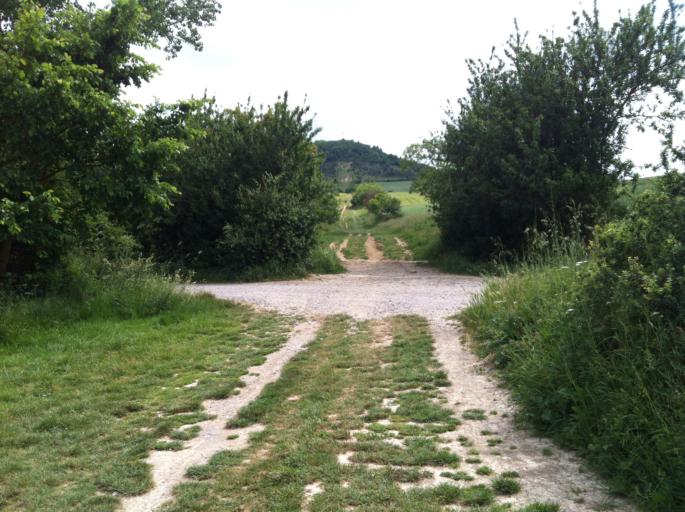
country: ES
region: Basque Country
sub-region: Provincia de Alava
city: Gasteiz / Vitoria
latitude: 42.8245
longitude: -2.6609
